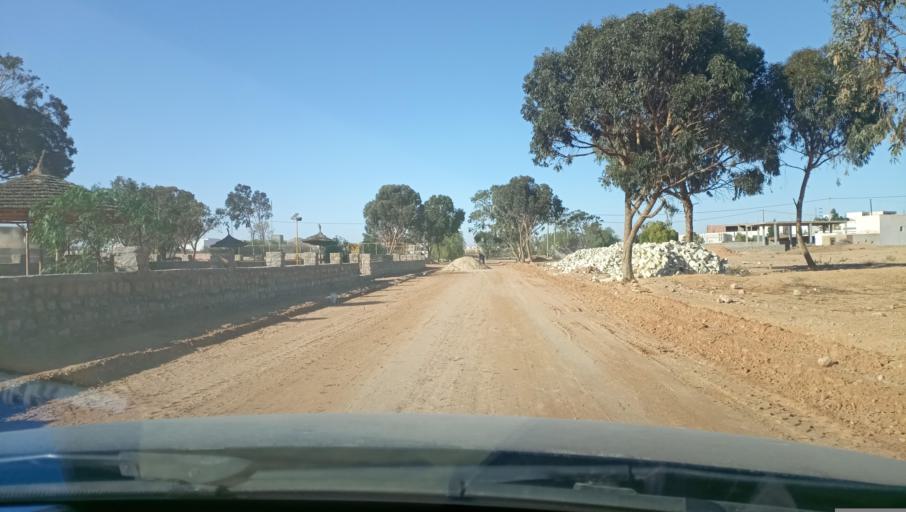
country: TN
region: Madanin
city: Medenine
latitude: 33.1811
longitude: 10.4393
